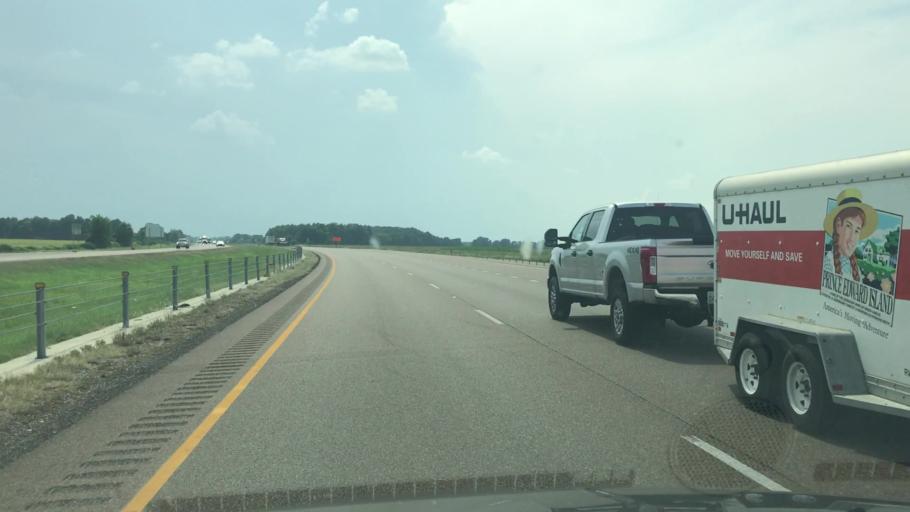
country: US
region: Arkansas
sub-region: Crittenden County
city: Earle
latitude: 35.1506
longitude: -90.4031
